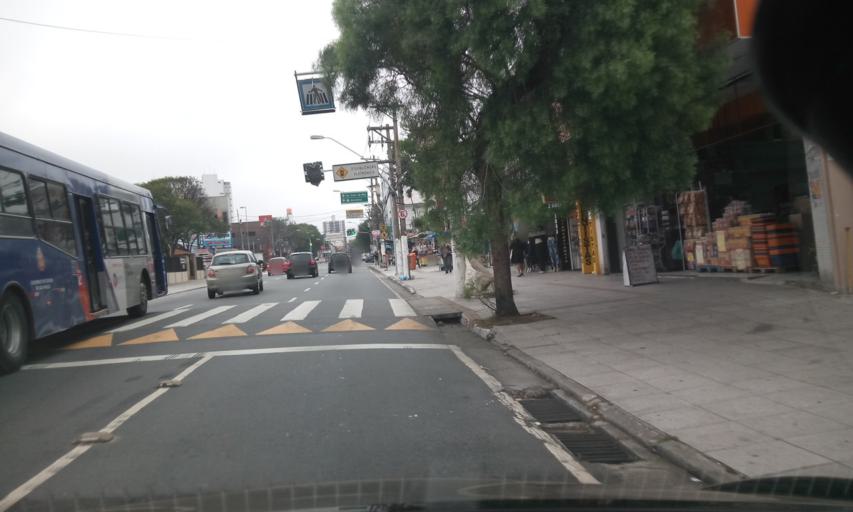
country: BR
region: Sao Paulo
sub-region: Santo Andre
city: Santo Andre
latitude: -23.6550
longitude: -46.5715
